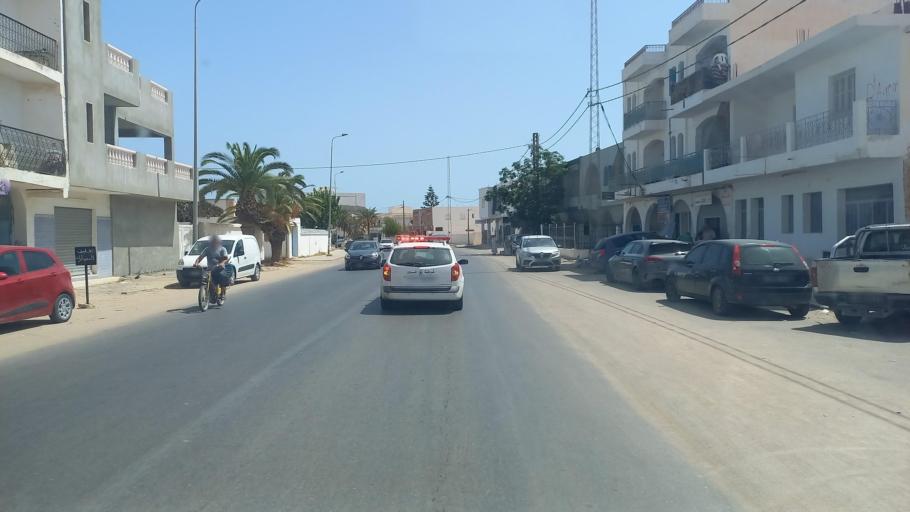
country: TN
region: Madanin
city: Zarzis
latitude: 33.4981
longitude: 11.0956
